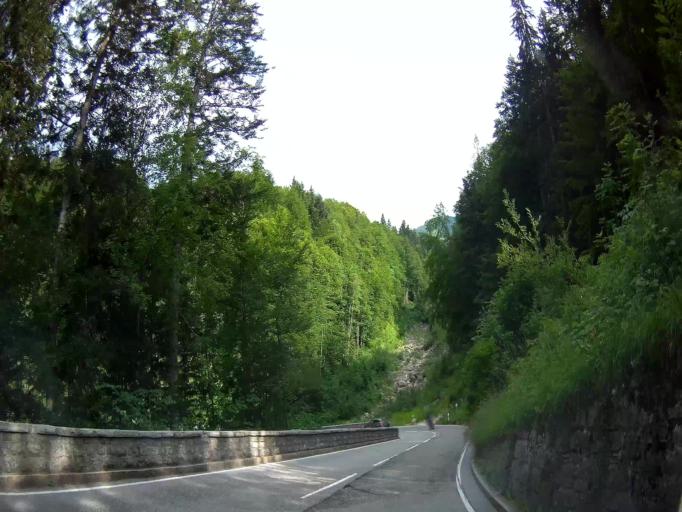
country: DE
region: Bavaria
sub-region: Upper Bavaria
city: Berchtesgaden
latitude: 47.6327
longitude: 13.0587
